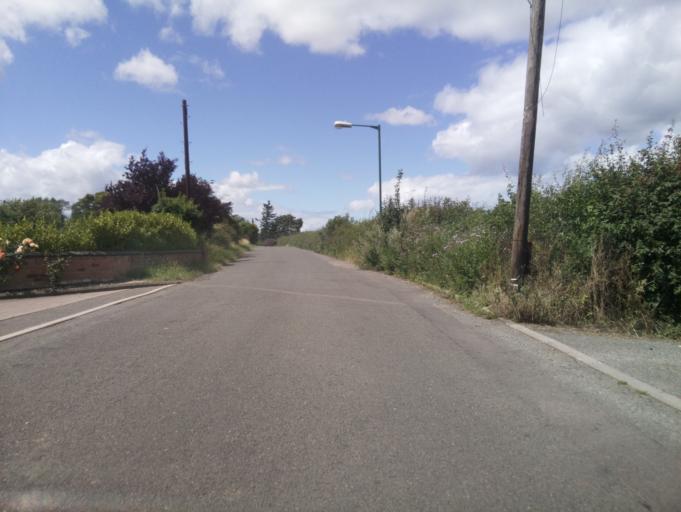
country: GB
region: England
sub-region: Nottinghamshire
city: Burton Joyce
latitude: 53.0059
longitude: -1.0809
